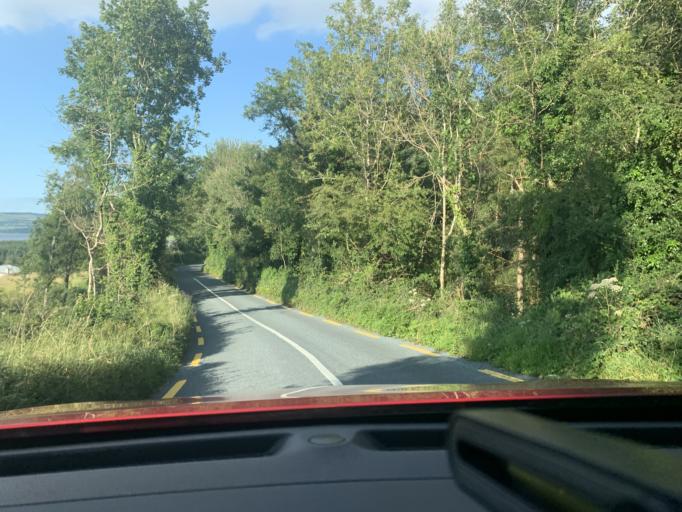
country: IE
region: Connaught
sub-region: Sligo
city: Strandhill
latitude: 54.1997
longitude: -8.5862
